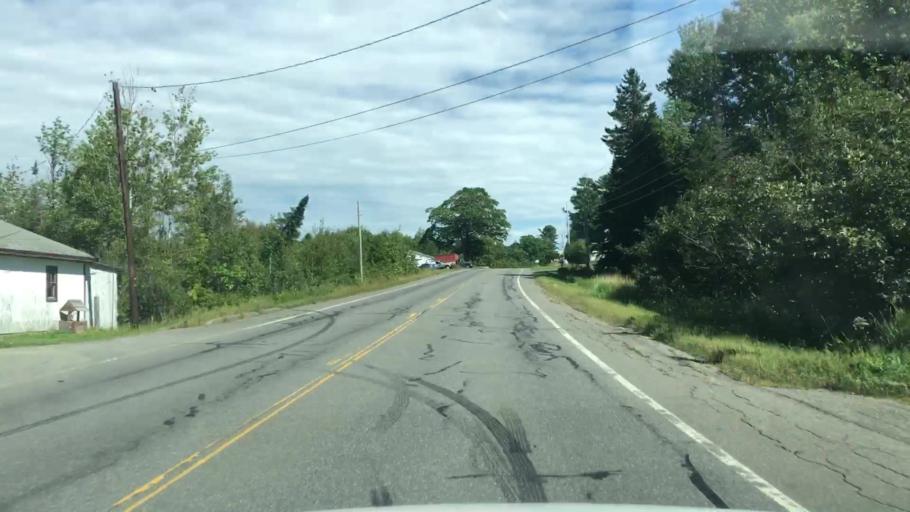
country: US
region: Maine
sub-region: Penobscot County
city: Garland
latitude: 45.0814
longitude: -69.2293
